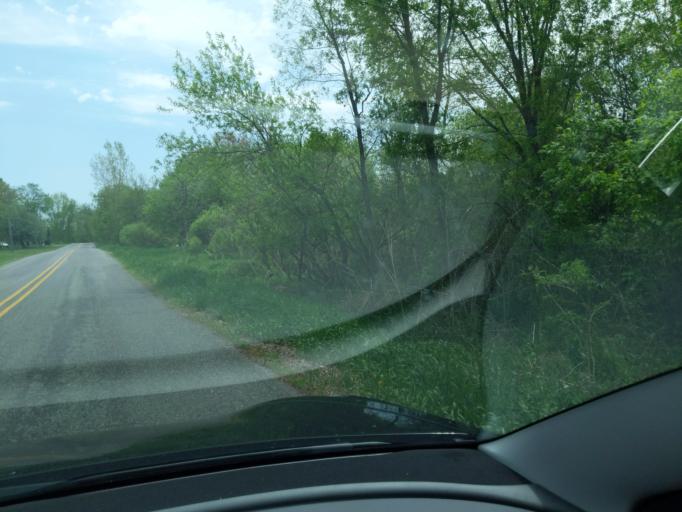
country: US
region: Michigan
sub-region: Ingham County
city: Stockbridge
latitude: 42.4750
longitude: -84.2313
